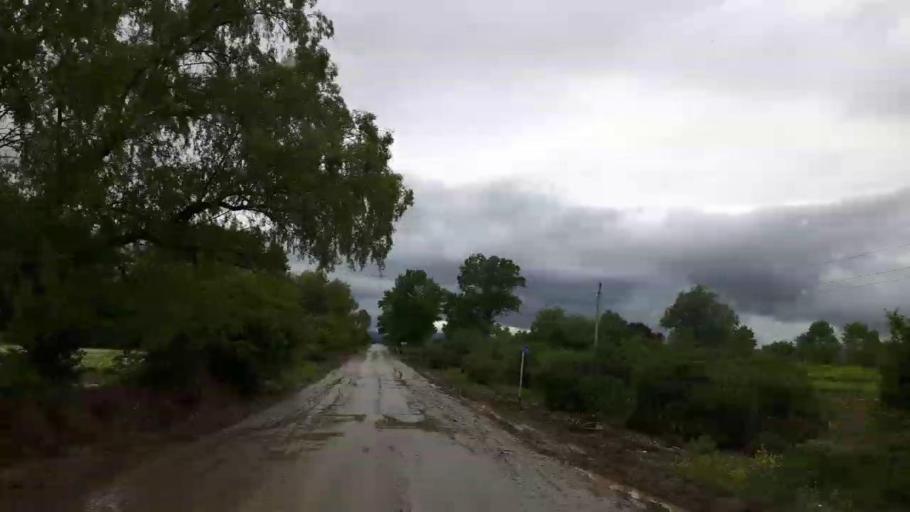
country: GE
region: Shida Kartli
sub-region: Khashuris Raioni
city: Khashuri
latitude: 41.9886
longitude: 43.7001
